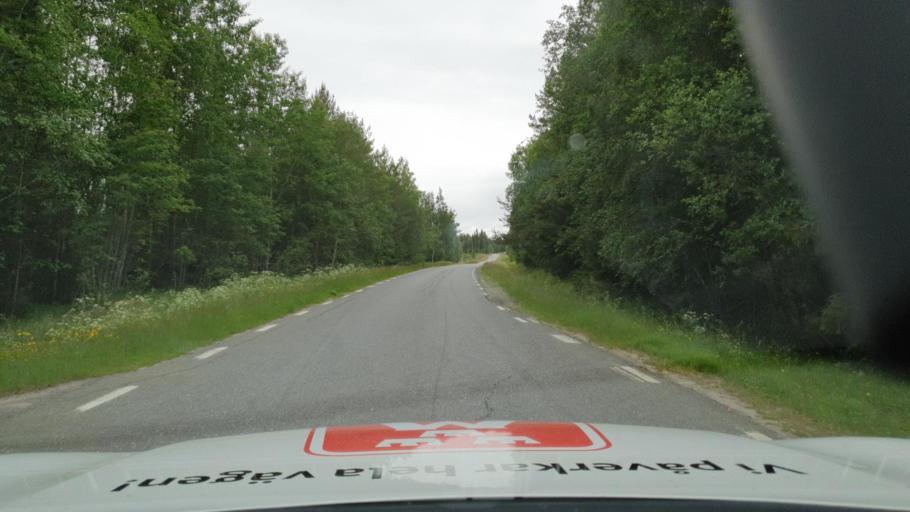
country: SE
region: Vaesterbotten
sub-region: Nordmalings Kommun
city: Nordmaling
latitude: 63.4815
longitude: 19.4531
